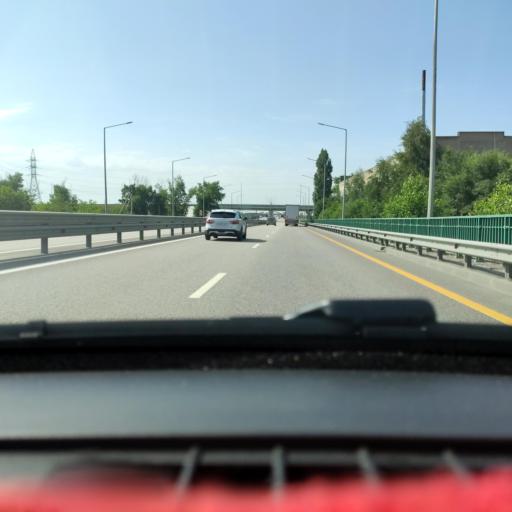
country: RU
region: Voronezj
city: Novaya Usman'
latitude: 51.6297
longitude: 39.3178
